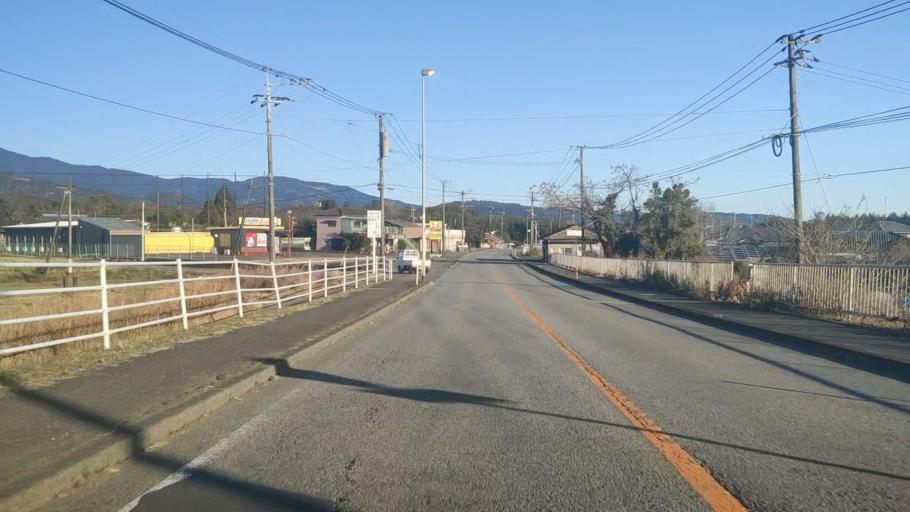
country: JP
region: Miyazaki
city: Takanabe
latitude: 32.2376
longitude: 131.5484
